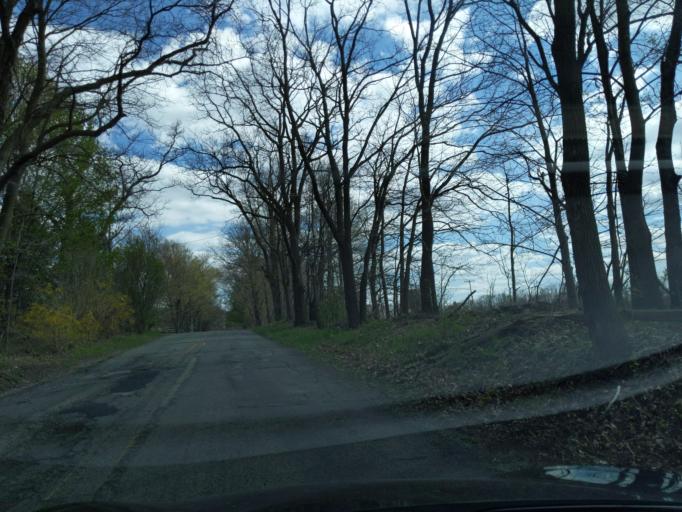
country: US
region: Michigan
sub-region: Ingham County
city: Leslie
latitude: 42.4355
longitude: -84.5263
